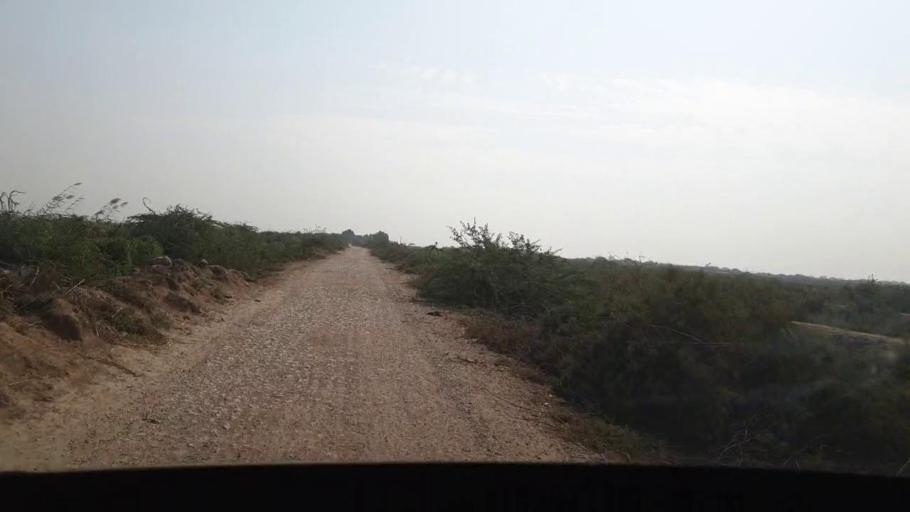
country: PK
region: Sindh
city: Chuhar Jamali
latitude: 24.2477
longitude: 67.9911
